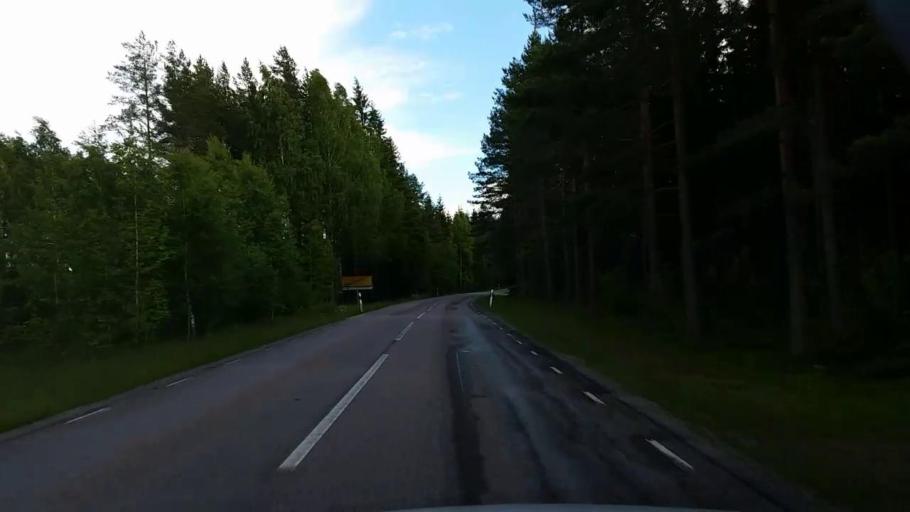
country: SE
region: Vaestmanland
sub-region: Fagersta Kommun
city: Fagersta
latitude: 59.9609
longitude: 15.7748
